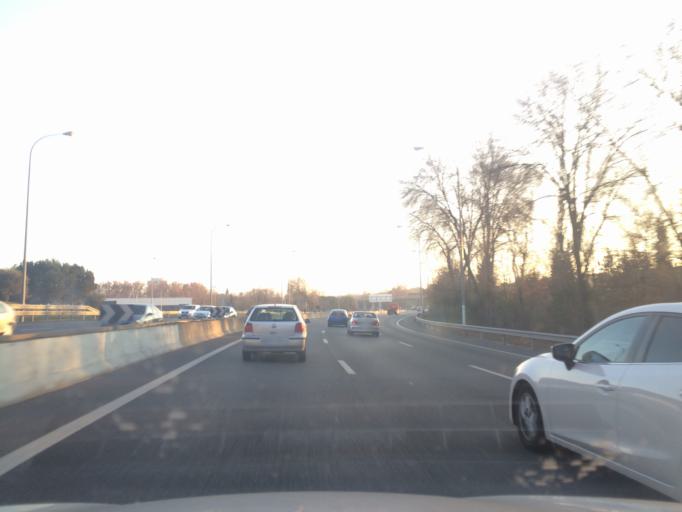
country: ES
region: Madrid
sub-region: Provincia de Madrid
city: Moncloa-Aravaca
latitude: 40.4382
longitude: -3.7379
